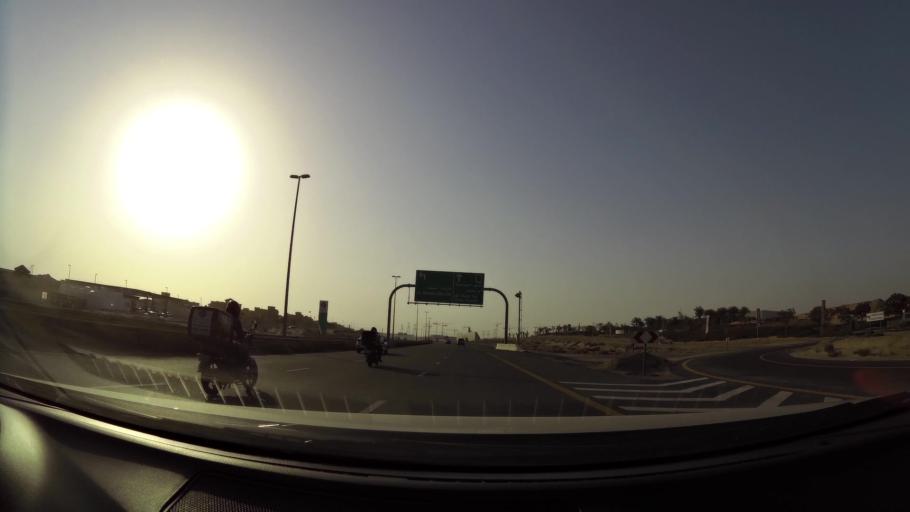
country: AE
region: Dubai
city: Dubai
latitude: 25.0918
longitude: 55.2451
